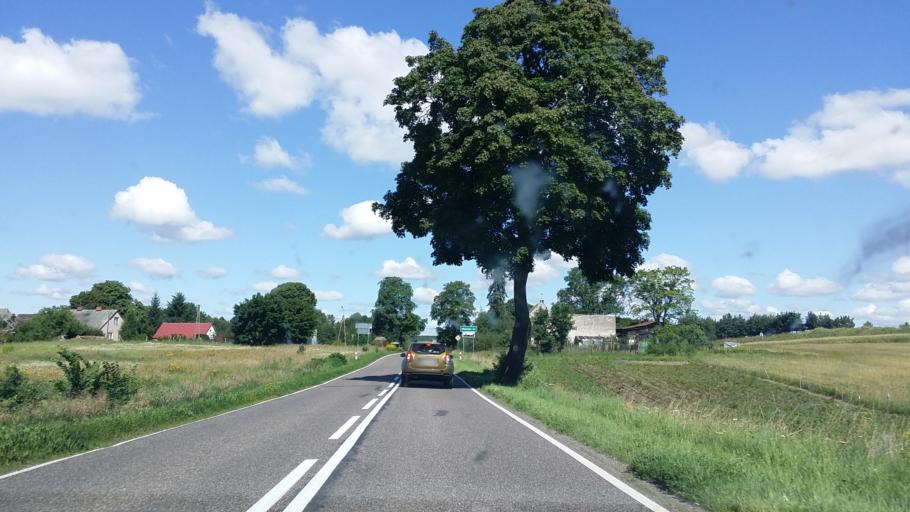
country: PL
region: West Pomeranian Voivodeship
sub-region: Powiat drawski
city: Drawsko Pomorskie
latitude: 53.4913
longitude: 15.8018
